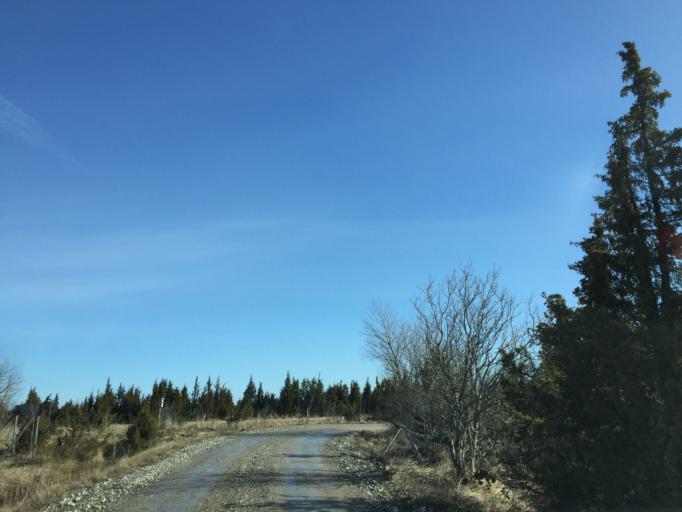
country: EE
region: Laeaene
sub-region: Haapsalu linn
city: Haapsalu
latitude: 58.6862
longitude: 23.5027
